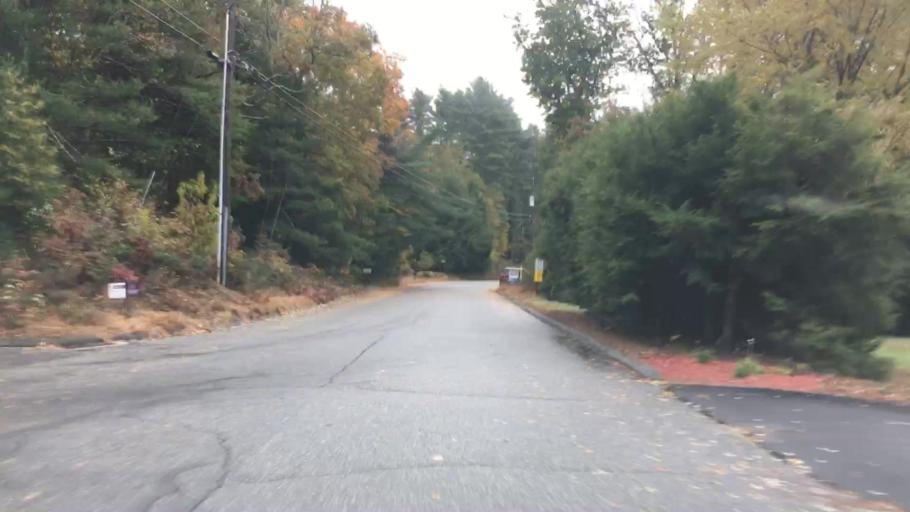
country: US
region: Connecticut
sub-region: Tolland County
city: Stafford Springs
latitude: 41.9823
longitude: -72.3283
